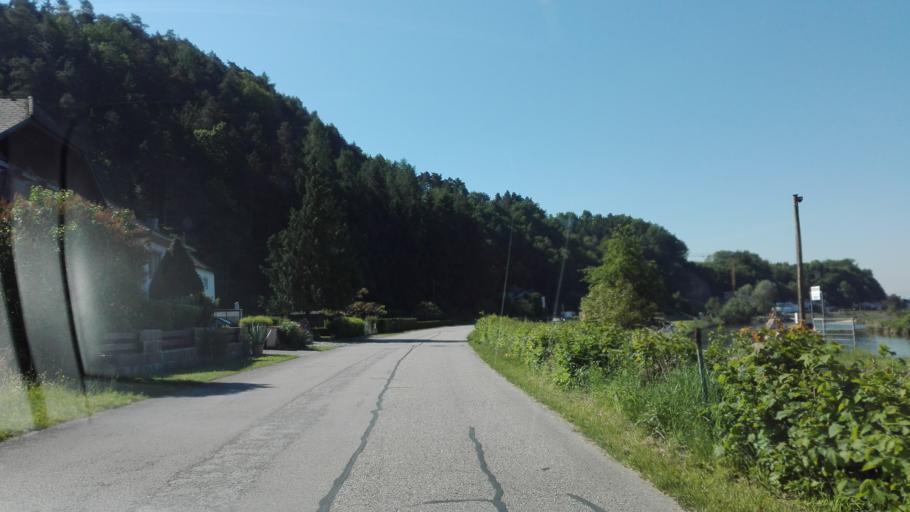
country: AT
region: Upper Austria
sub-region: Politischer Bezirk Urfahr-Umgebung
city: Feldkirchen an der Donau
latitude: 48.3733
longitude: 14.0332
